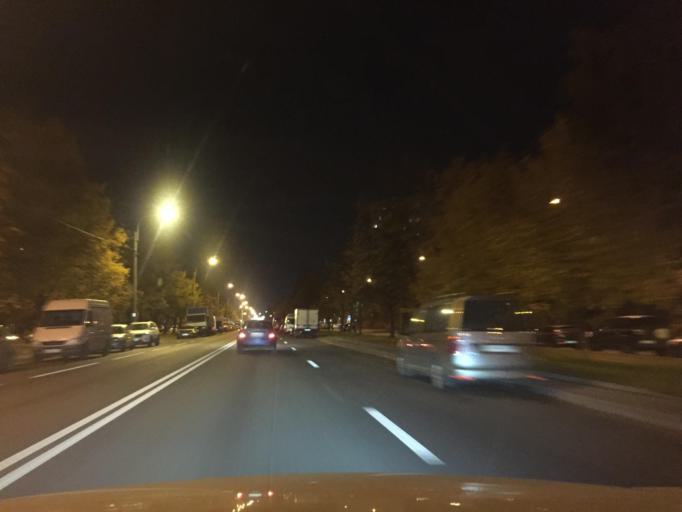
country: RU
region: Leningrad
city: Akademicheskoe
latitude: 60.0102
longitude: 30.4271
